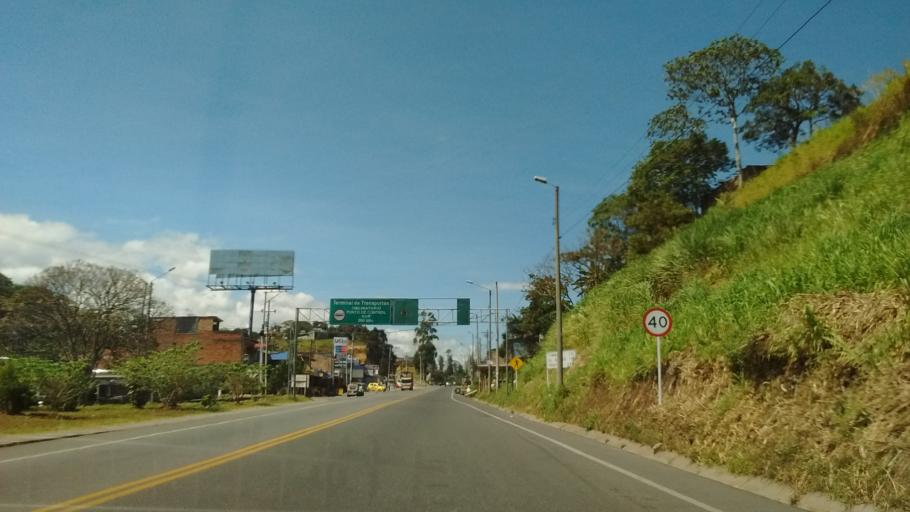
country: CO
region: Cauca
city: Popayan
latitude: 2.4301
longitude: -76.6209
